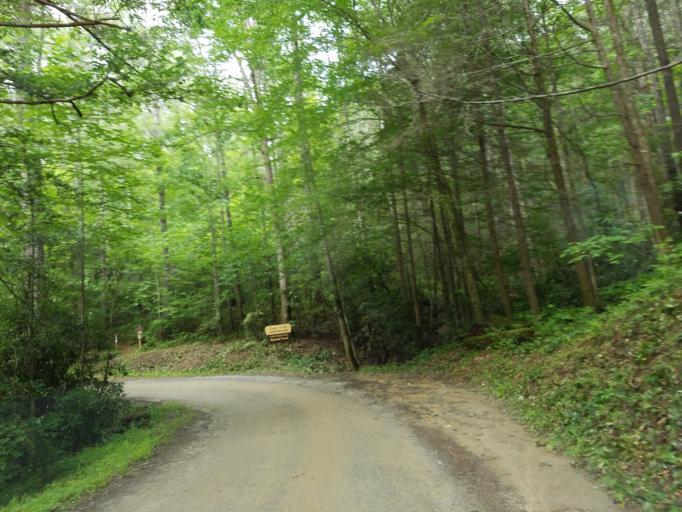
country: US
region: Georgia
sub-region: Union County
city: Blairsville
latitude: 34.7618
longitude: -84.0676
